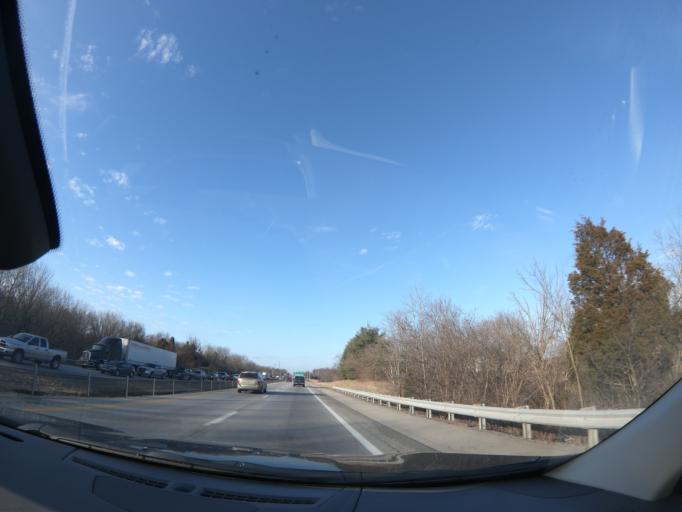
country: US
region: Kentucky
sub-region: Jefferson County
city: Middletown
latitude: 38.2155
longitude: -85.5062
